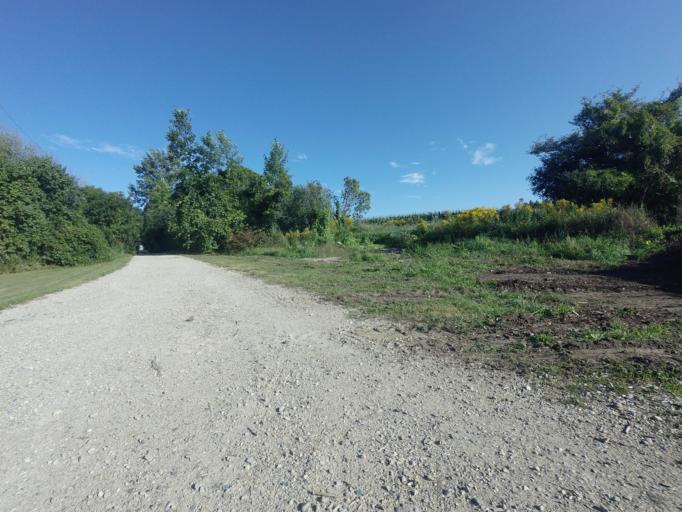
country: CA
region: Ontario
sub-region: Wellington County
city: Guelph
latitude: 43.6630
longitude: -80.4327
